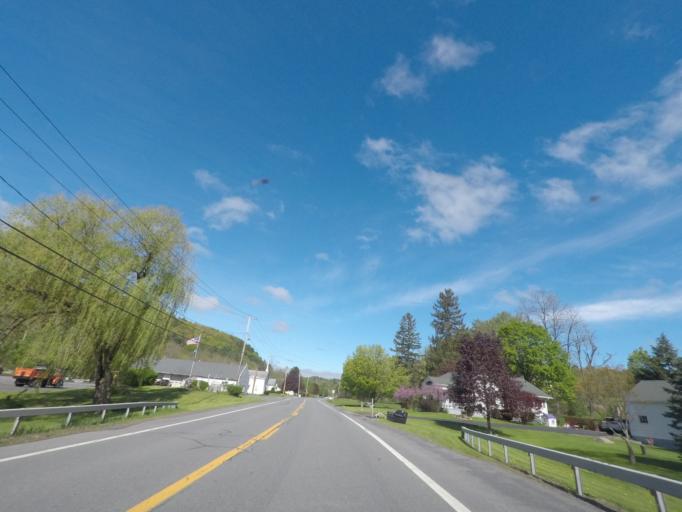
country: US
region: New York
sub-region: Albany County
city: Ravena
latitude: 42.4719
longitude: -73.8956
